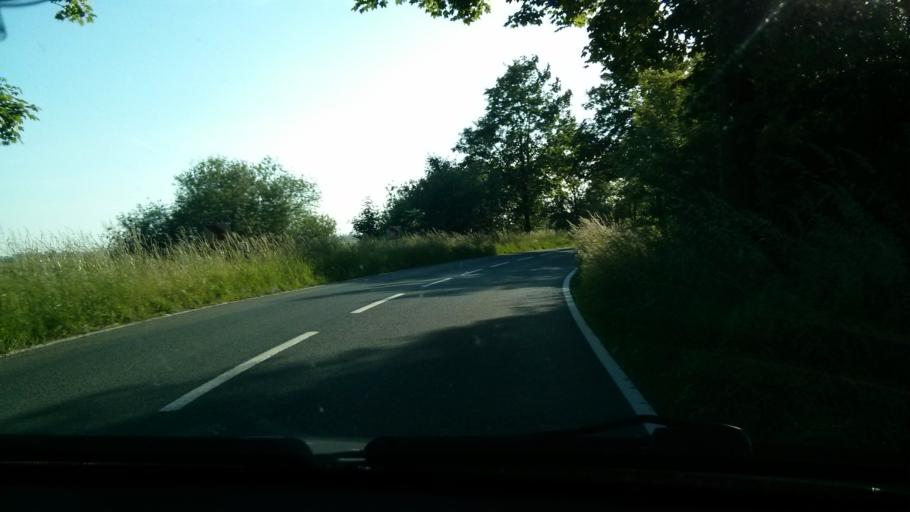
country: DE
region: Bremen
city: Bremerhaven
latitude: 53.4777
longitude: 8.5735
